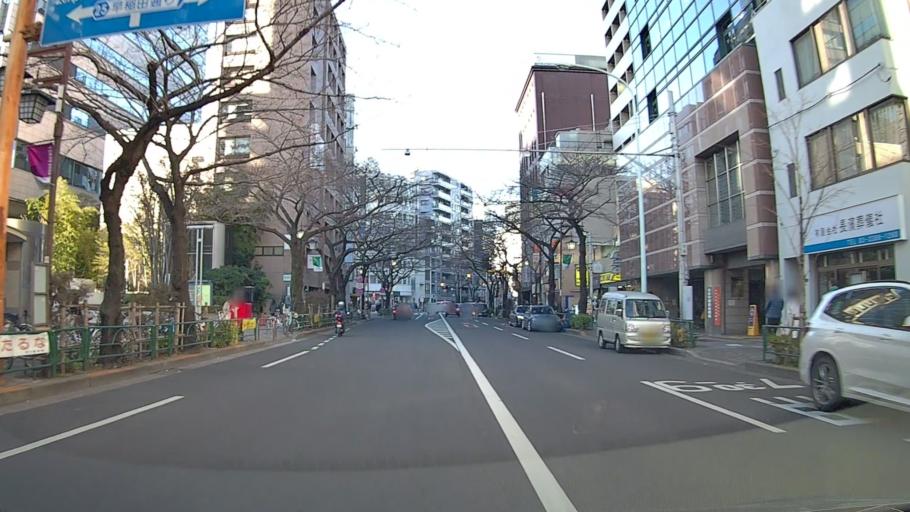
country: JP
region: Tokyo
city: Tokyo
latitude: 35.7089
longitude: 139.6651
